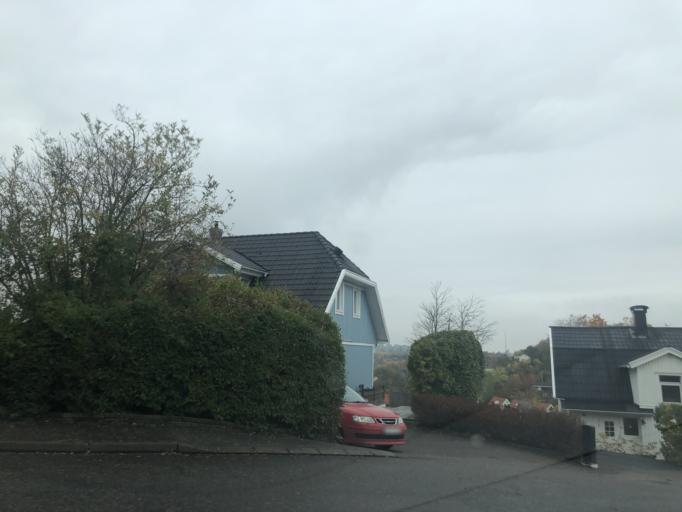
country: SE
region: Vaestra Goetaland
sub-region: Goteborg
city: Majorna
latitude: 57.6313
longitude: 11.9205
